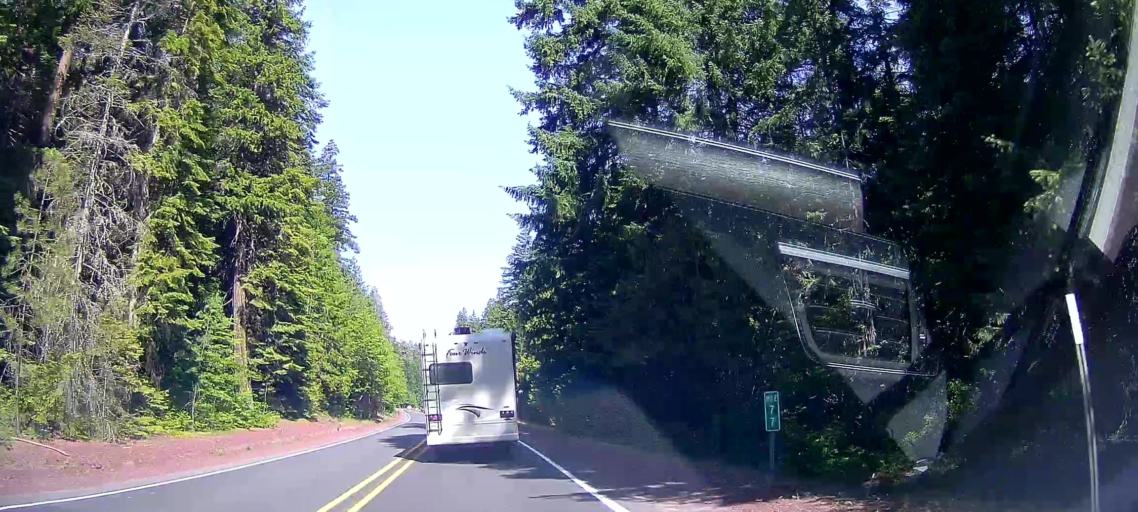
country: US
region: Oregon
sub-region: Jefferson County
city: Warm Springs
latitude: 45.0721
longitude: -121.5307
